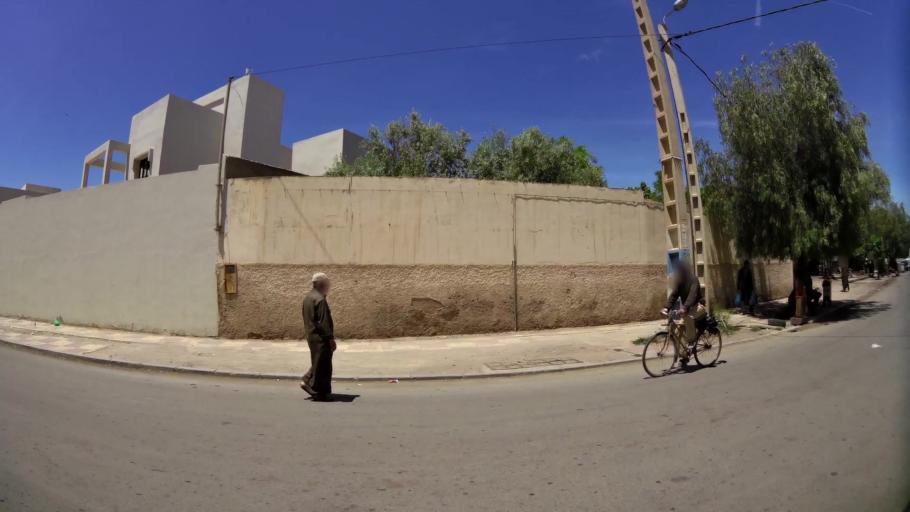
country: MA
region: Oriental
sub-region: Oujda-Angad
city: Oujda
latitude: 34.6749
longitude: -1.9279
